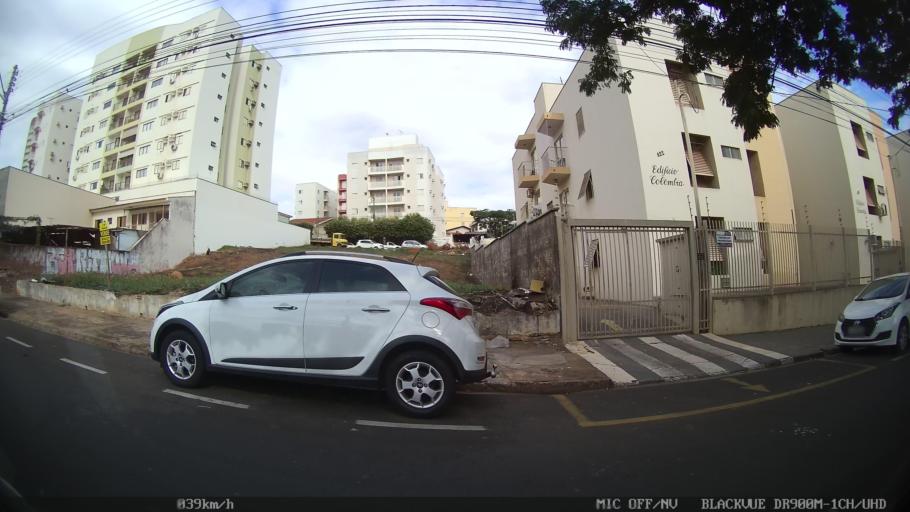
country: BR
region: Sao Paulo
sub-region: Sao Jose Do Rio Preto
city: Sao Jose do Rio Preto
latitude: -20.8320
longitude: -49.3847
